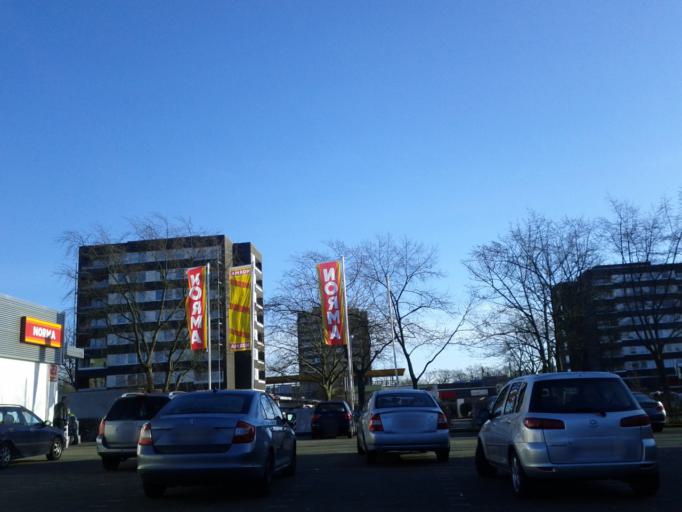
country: DE
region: North Rhine-Westphalia
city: Lanstrop
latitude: 51.5522
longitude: 7.5402
